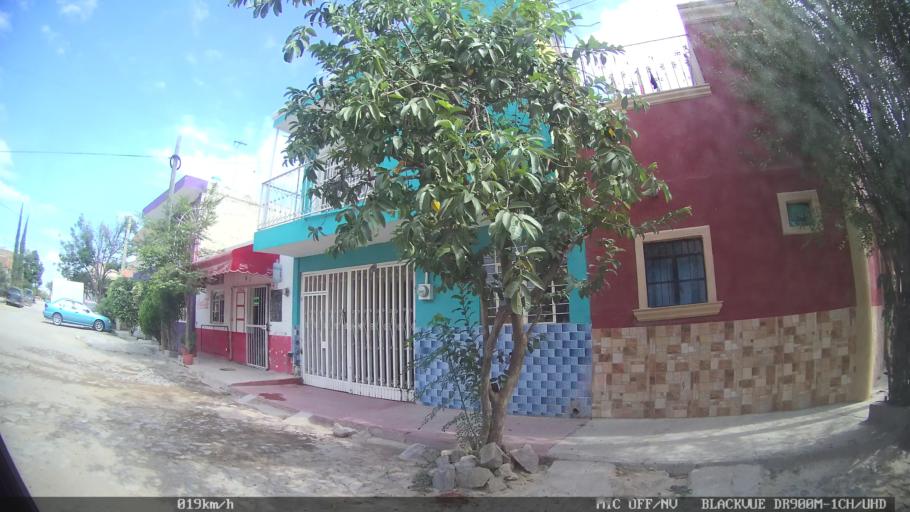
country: MX
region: Jalisco
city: Tlaquepaque
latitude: 20.6831
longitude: -103.2549
